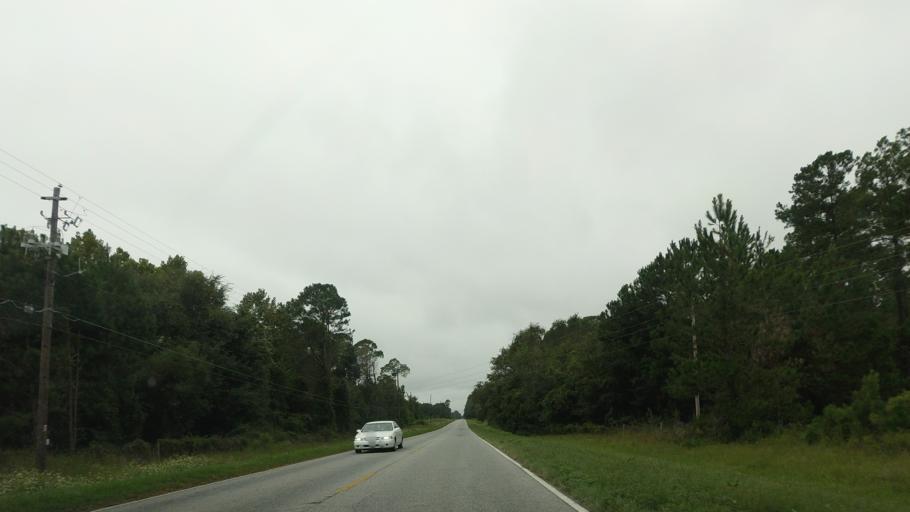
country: US
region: Georgia
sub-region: Lowndes County
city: Valdosta
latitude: 30.8133
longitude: -83.2406
